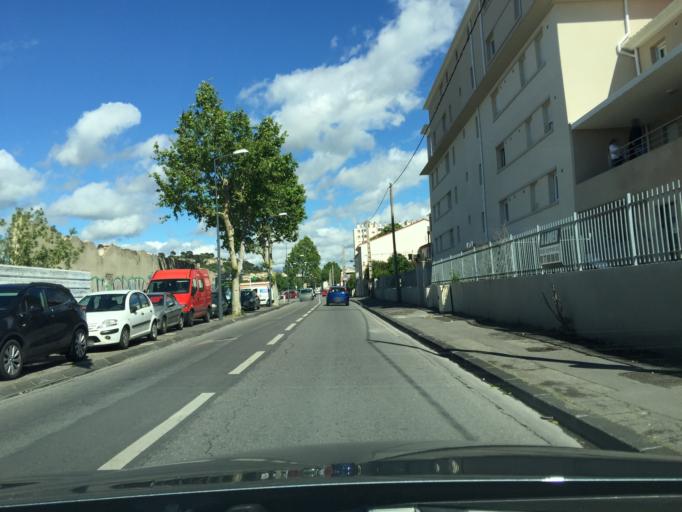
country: FR
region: Provence-Alpes-Cote d'Azur
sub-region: Departement des Bouches-du-Rhone
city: Marseille 11
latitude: 43.2886
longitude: 5.4558
